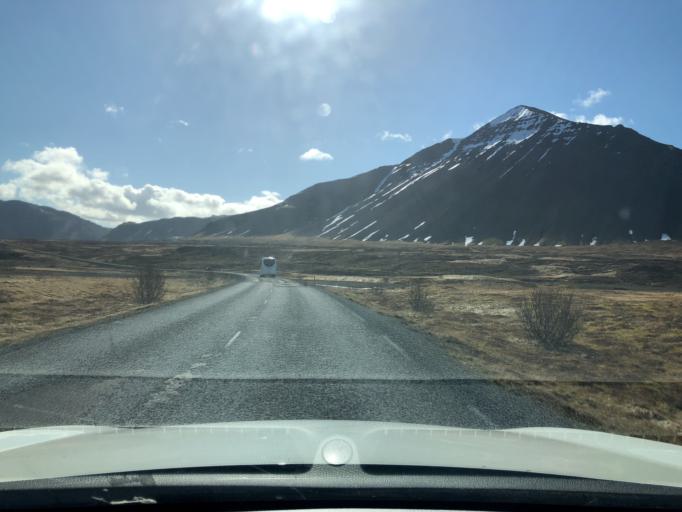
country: IS
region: West
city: Borgarnes
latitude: 64.5246
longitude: -21.8743
